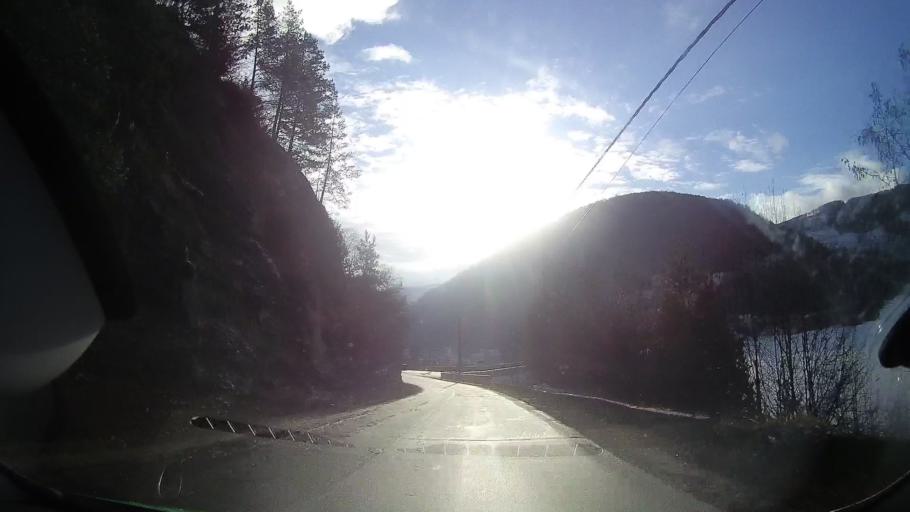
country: RO
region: Alba
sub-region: Comuna Sohodol
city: Sohodol
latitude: 46.3743
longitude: 23.0184
